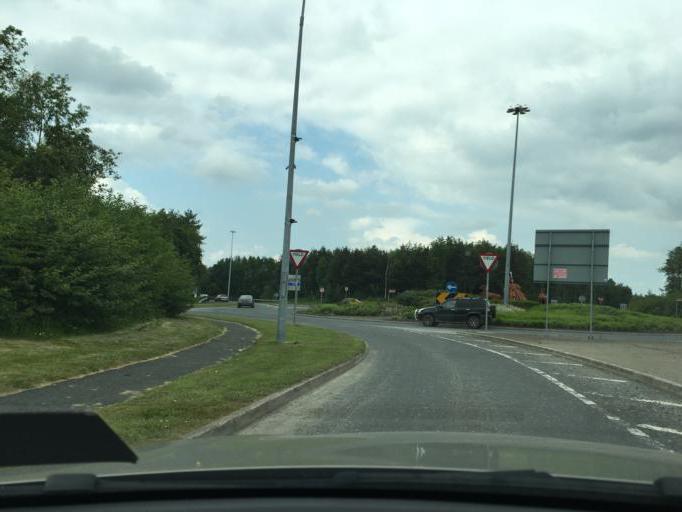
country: IE
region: Leinster
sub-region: Kildare
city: Athgarvan
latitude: 53.1607
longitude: -6.8240
